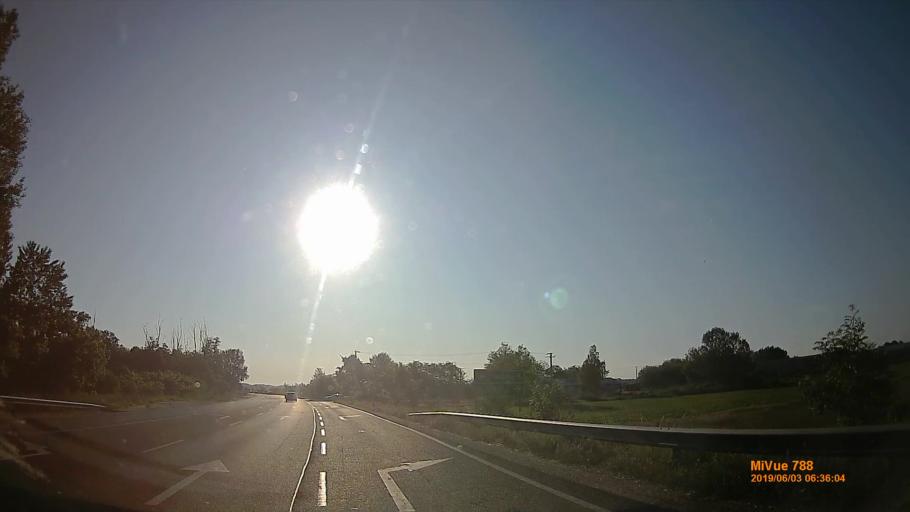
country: HU
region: Pest
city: Taksony
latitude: 47.3085
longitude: 19.0805
